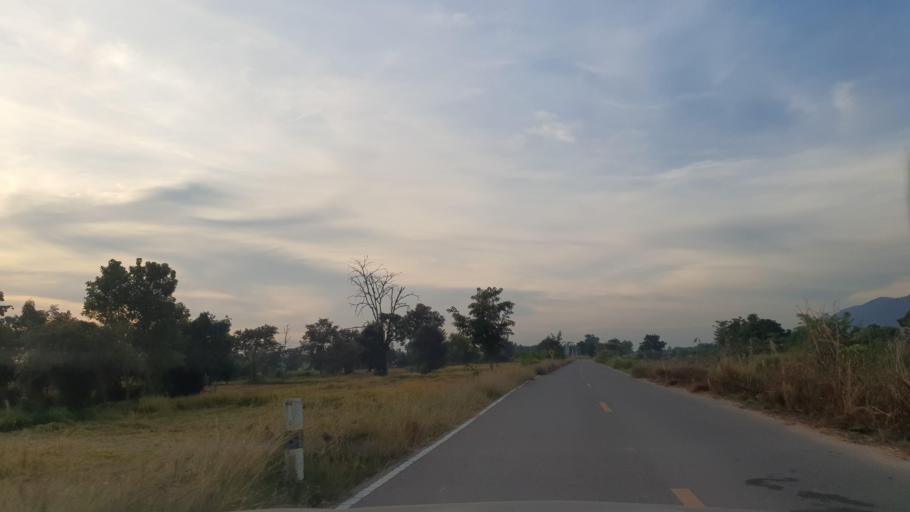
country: TH
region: Uthai Thani
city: Sawang Arom
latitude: 15.7128
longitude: 99.9569
